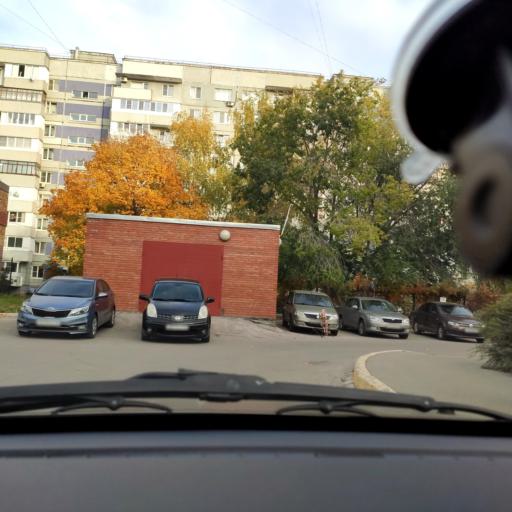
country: RU
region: Samara
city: Tol'yatti
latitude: 53.5406
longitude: 49.3351
